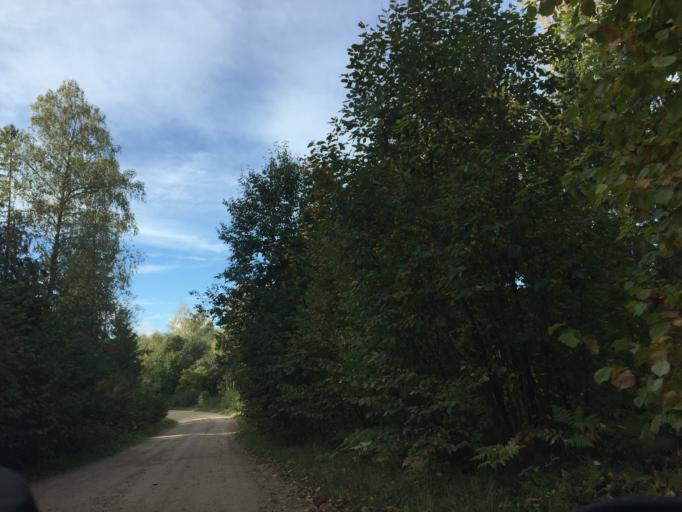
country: LV
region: Jaunpils
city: Jaunpils
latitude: 56.6099
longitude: 23.0061
